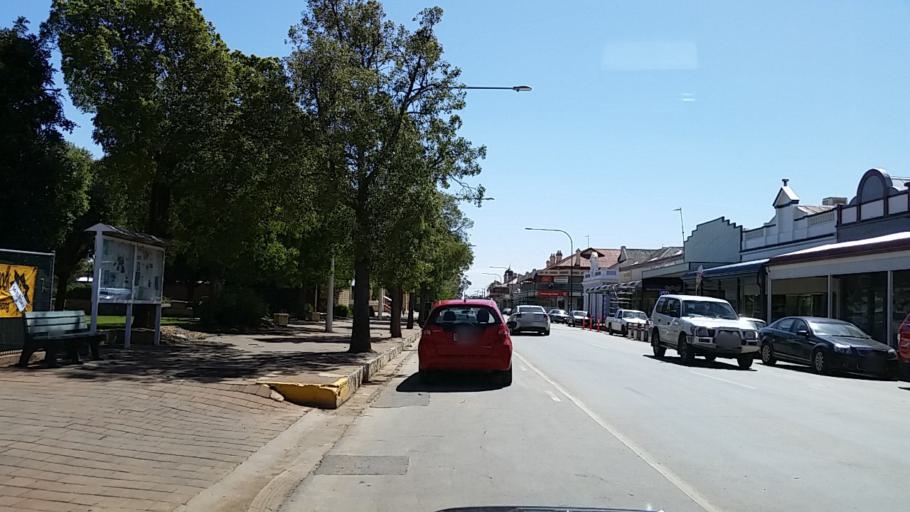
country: AU
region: South Australia
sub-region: Peterborough
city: Peterborough
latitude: -32.9734
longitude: 138.8376
